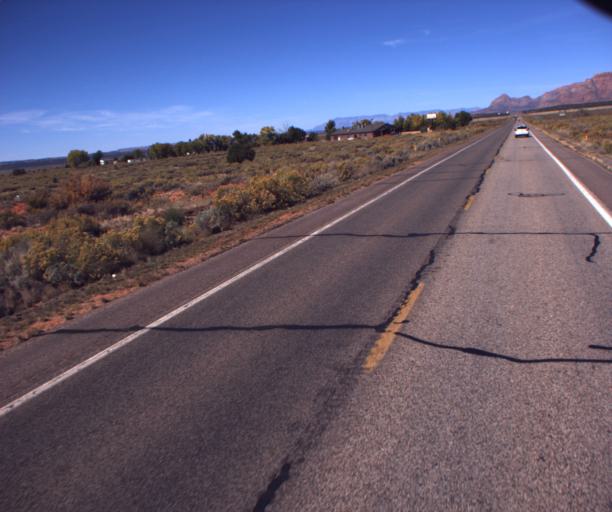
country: US
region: Arizona
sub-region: Mohave County
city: Colorado City
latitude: 36.9286
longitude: -112.9418
